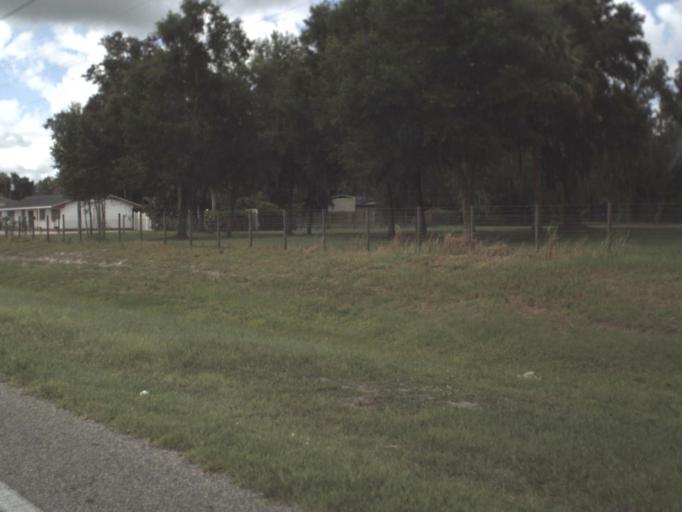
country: US
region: Florida
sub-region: Hardee County
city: Wauchula
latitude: 27.5659
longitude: -81.8153
